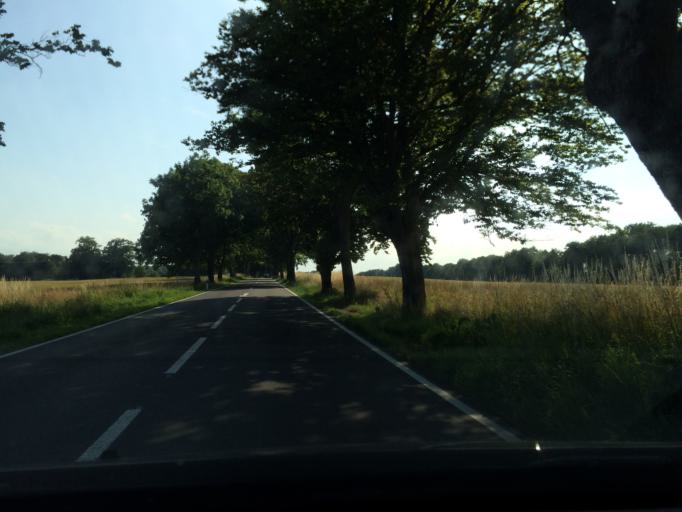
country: DE
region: Mecklenburg-Vorpommern
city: Ostseebad Binz
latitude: 54.4153
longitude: 13.5383
